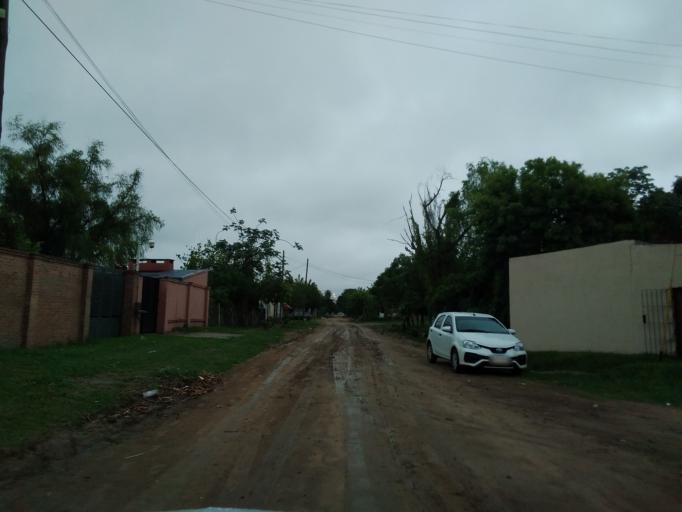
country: AR
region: Corrientes
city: Corrientes
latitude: -27.4885
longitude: -58.8202
